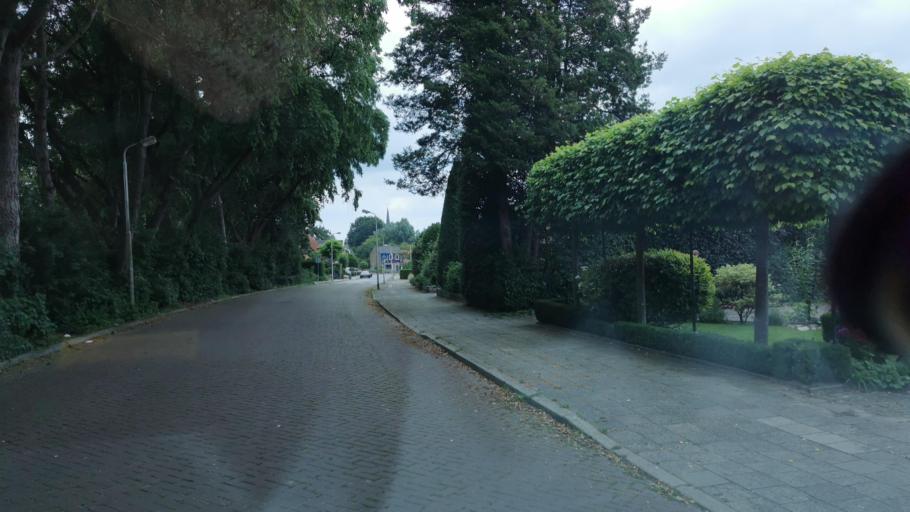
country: NL
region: Overijssel
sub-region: Gemeente Losser
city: Losser
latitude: 52.2594
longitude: 7.0050
